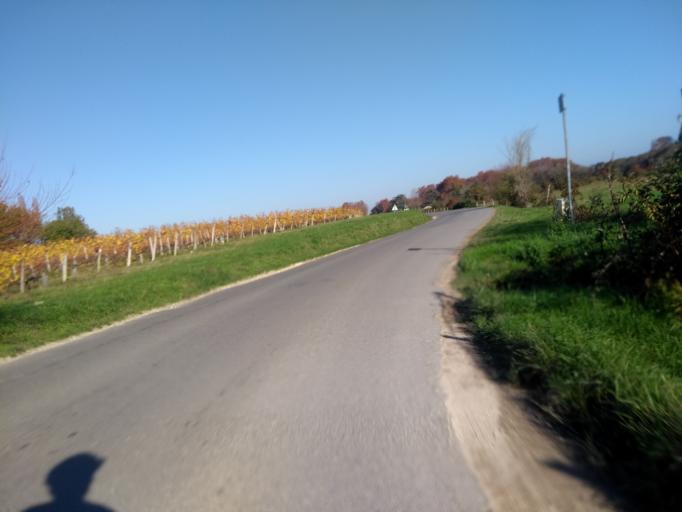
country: FR
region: Aquitaine
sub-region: Departement de la Gironde
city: Martillac
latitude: 44.6929
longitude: -0.5179
